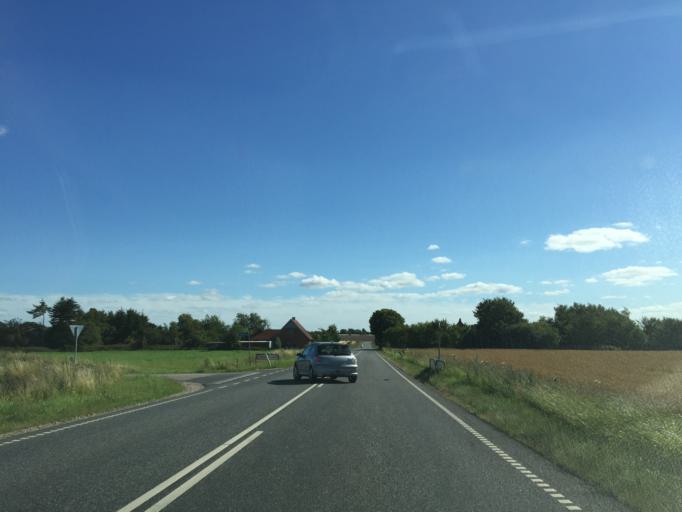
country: DK
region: Central Jutland
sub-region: Viborg Kommune
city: Bjerringbro
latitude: 56.3428
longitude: 9.6801
